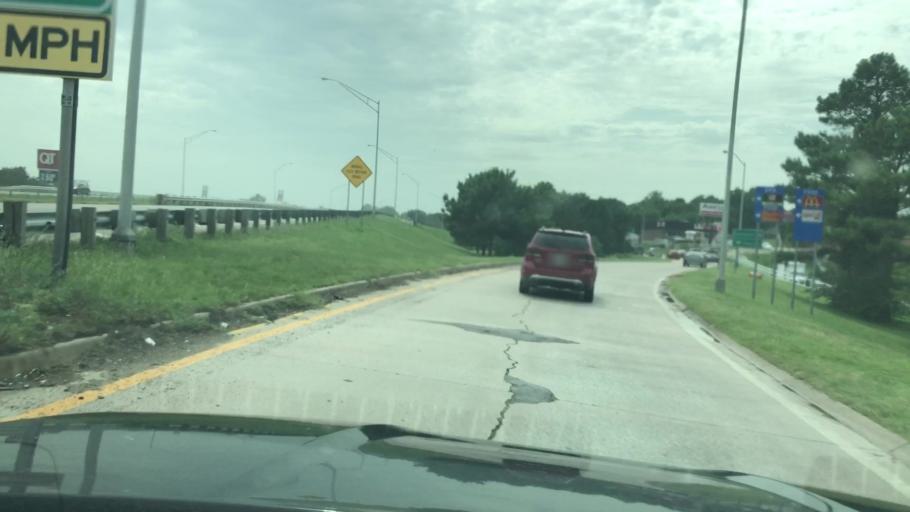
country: US
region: Oklahoma
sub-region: Tulsa County
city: Sand Springs
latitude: 36.1370
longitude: -96.1134
